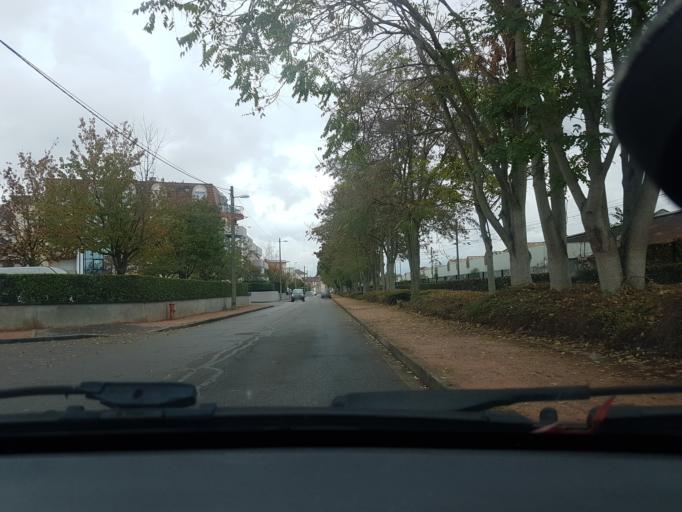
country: FR
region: Bourgogne
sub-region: Departement de la Cote-d'Or
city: Saint-Apollinaire
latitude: 47.3263
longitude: 5.0568
